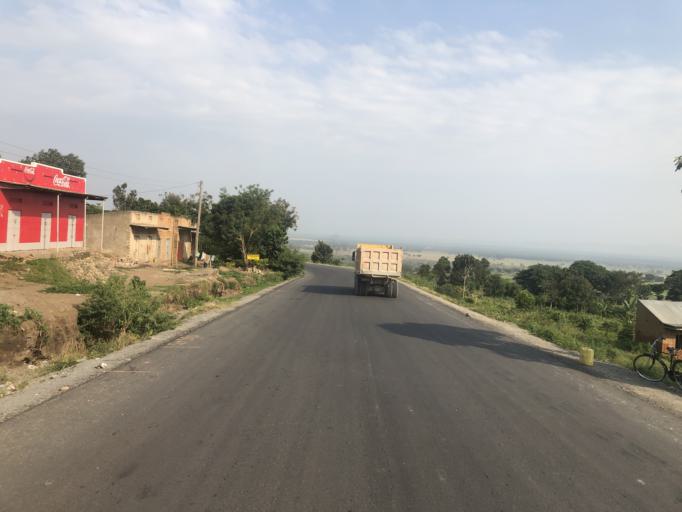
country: UG
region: Western Region
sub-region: Rubirizi District
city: Rubirizi
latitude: -0.2133
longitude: 30.1015
